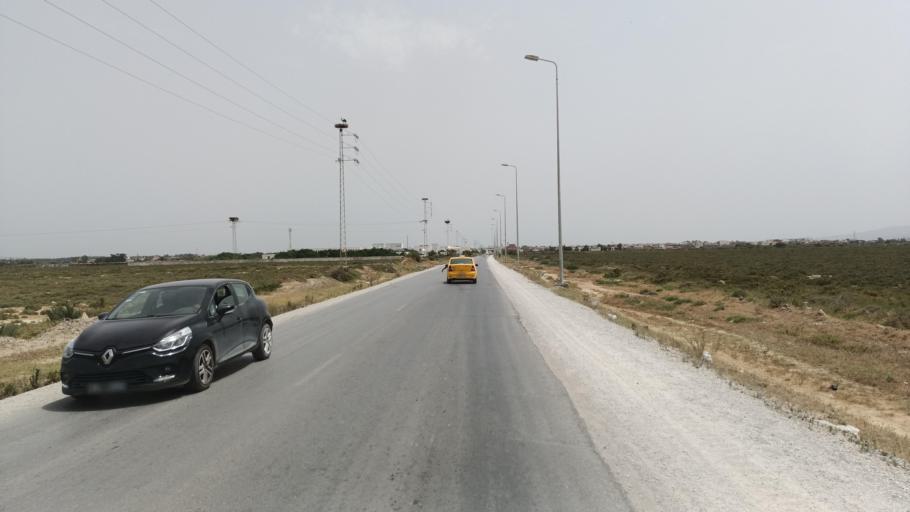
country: TN
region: Nabul
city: Manzil Bu Zalafah
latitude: 36.7163
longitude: 10.4780
